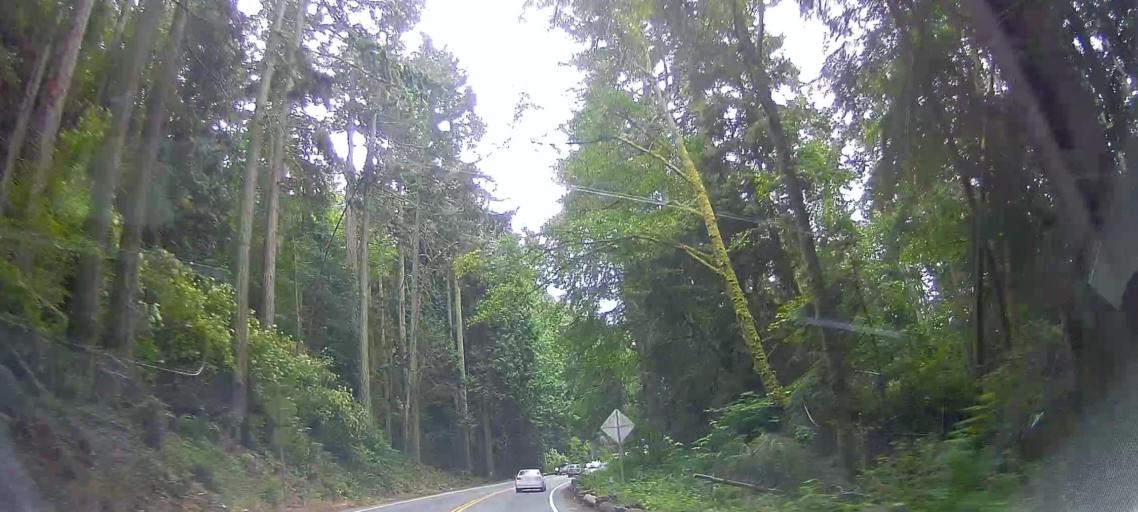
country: US
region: Washington
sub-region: Island County
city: Ault Field
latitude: 48.4152
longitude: -122.6462
